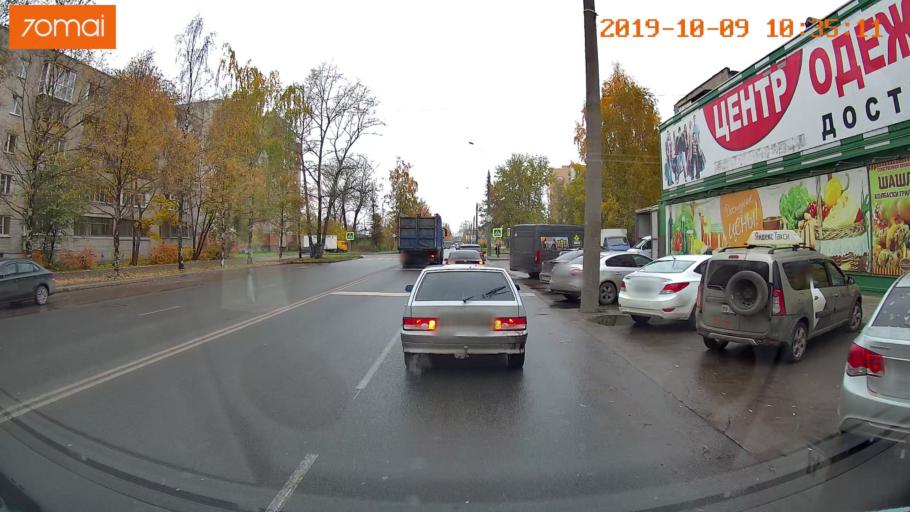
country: RU
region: Vologda
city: Vologda
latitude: 59.2264
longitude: 39.8645
